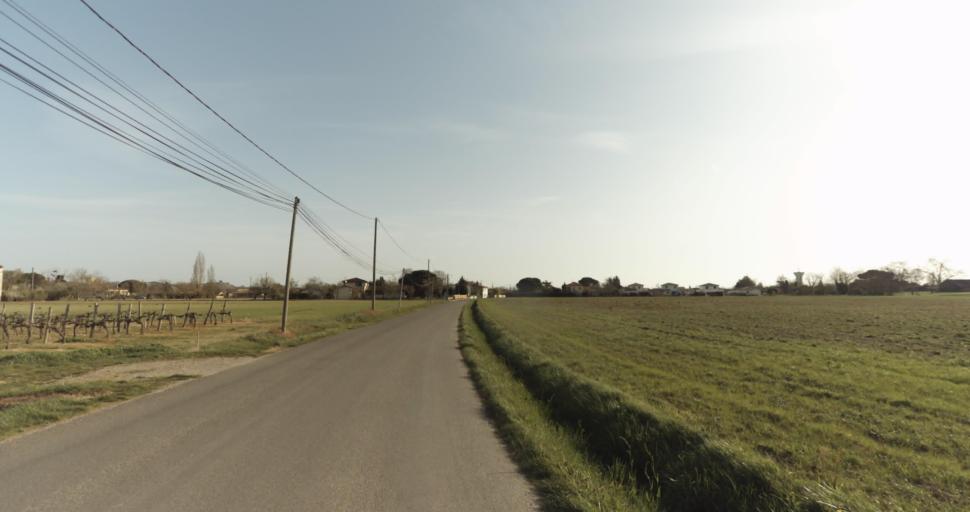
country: FR
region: Midi-Pyrenees
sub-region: Departement du Tarn
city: Saint-Sulpice-la-Pointe
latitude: 43.7669
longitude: 1.6773
